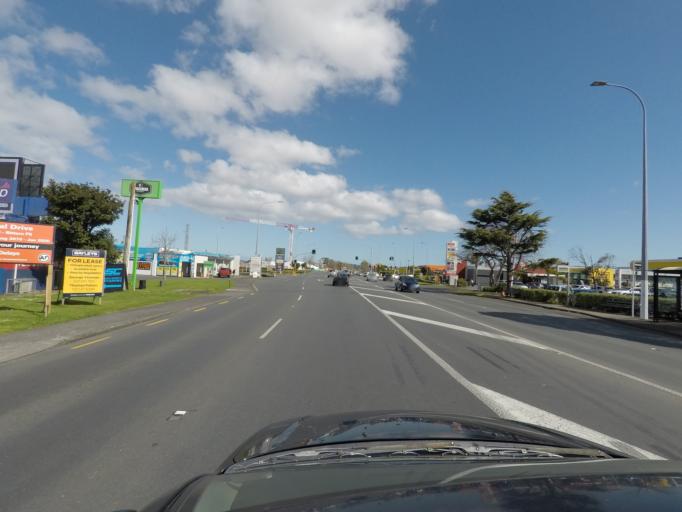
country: NZ
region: Auckland
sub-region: Auckland
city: Rosebank
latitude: -36.8559
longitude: 174.6300
